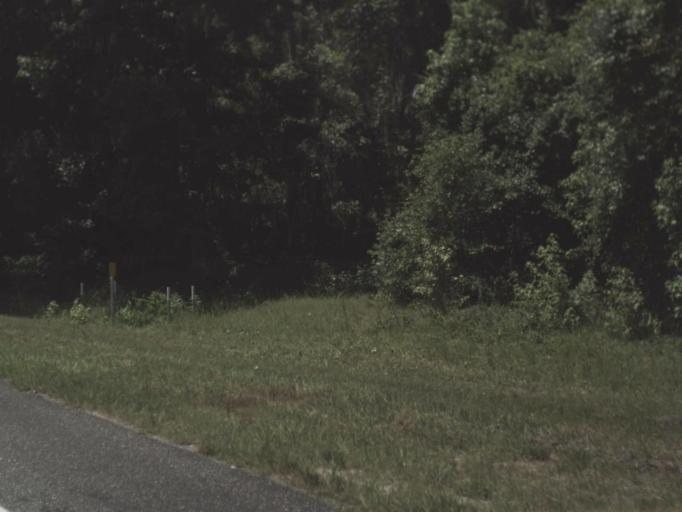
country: US
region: Florida
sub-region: Putnam County
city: Crescent City
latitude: 29.4692
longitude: -81.5296
